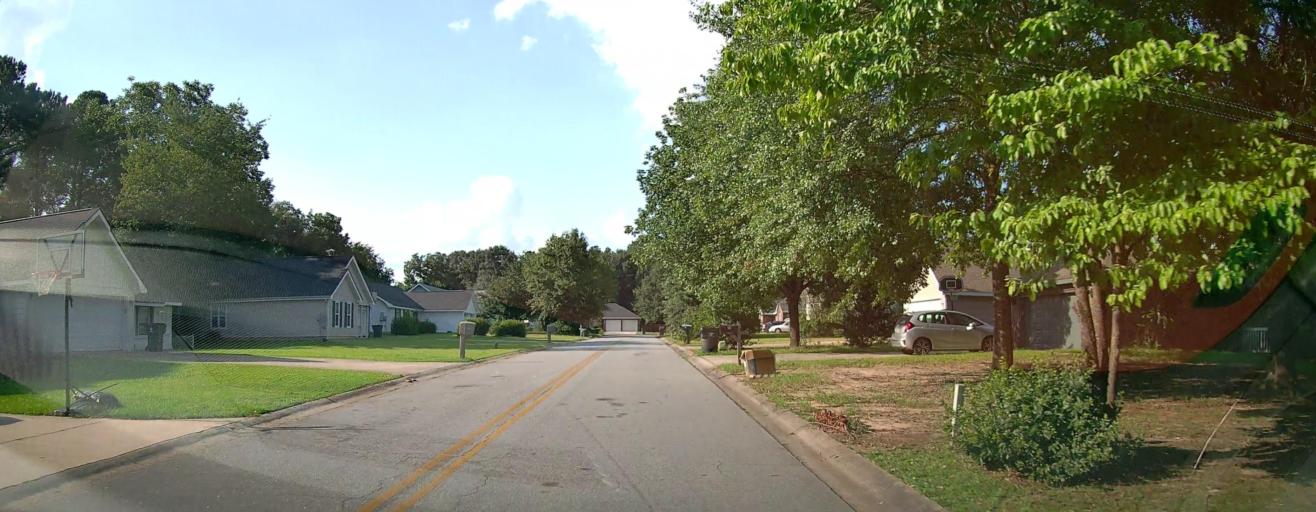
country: US
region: Georgia
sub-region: Houston County
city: Warner Robins
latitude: 32.5883
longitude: -83.6413
